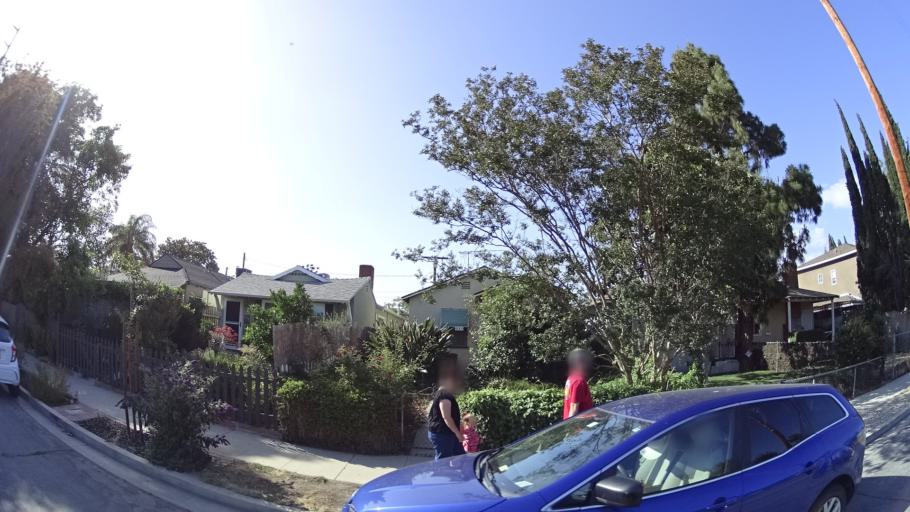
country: US
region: California
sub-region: Los Angeles County
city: North Hollywood
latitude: 34.1704
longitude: -118.3519
